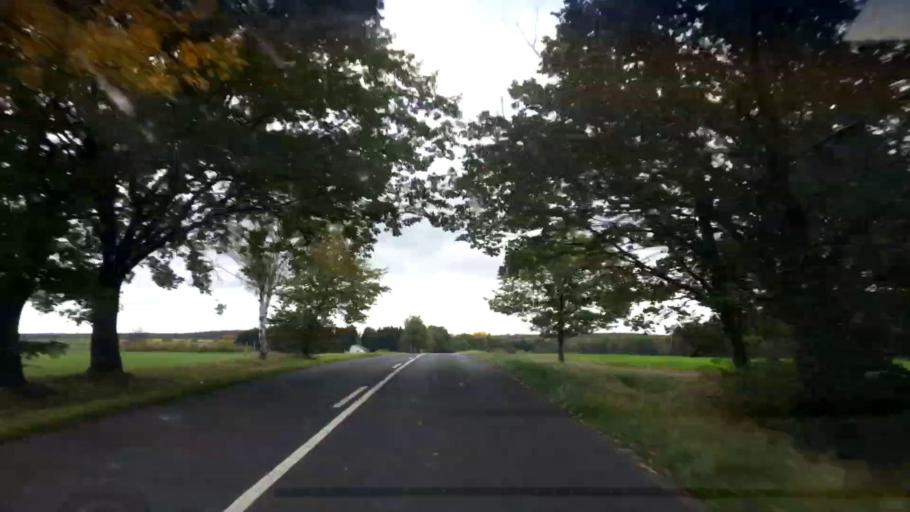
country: DE
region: Bavaria
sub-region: Upper Palatinate
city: Waldsassen
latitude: 50.0173
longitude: 12.3205
